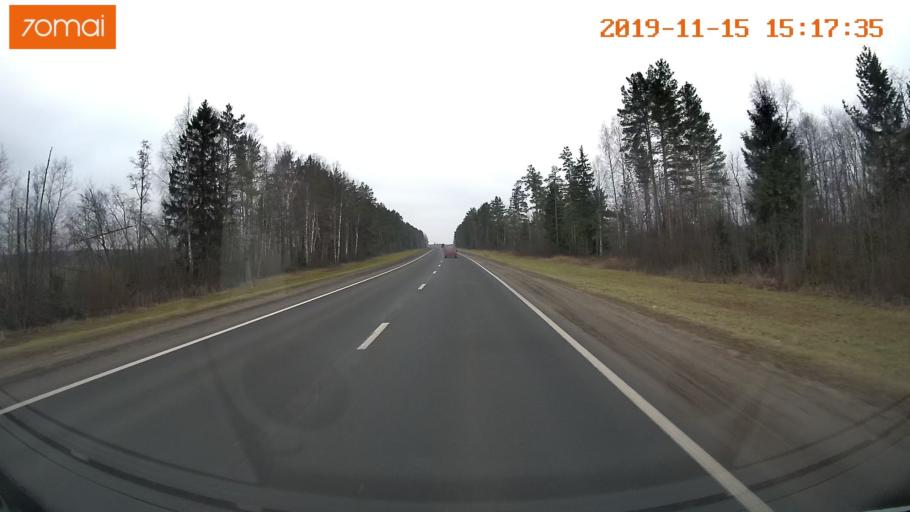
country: RU
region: Jaroslavl
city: Danilov
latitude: 58.2589
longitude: 40.1811
